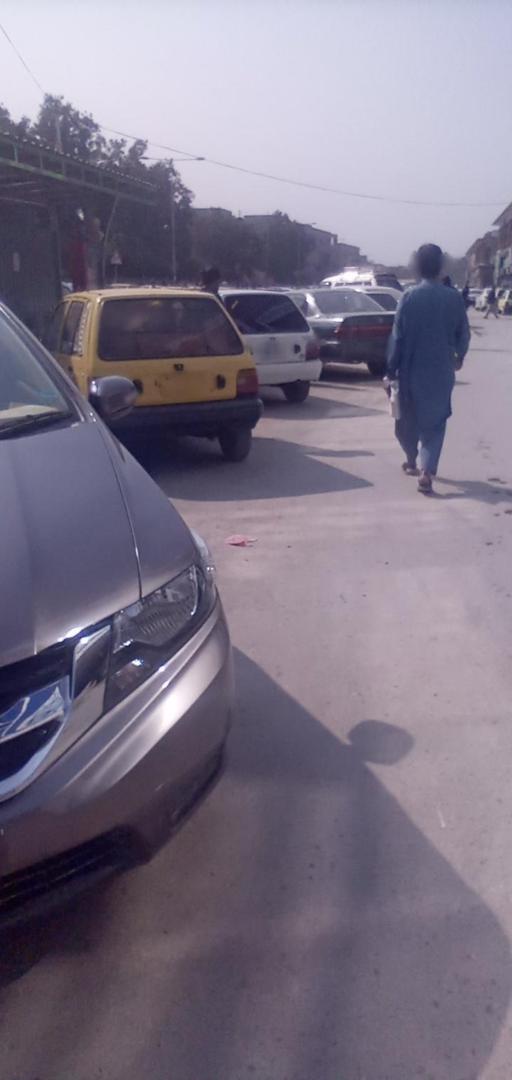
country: PK
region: Khyber Pakhtunkhwa
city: Peshawar
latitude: 33.9940
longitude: 71.4516
